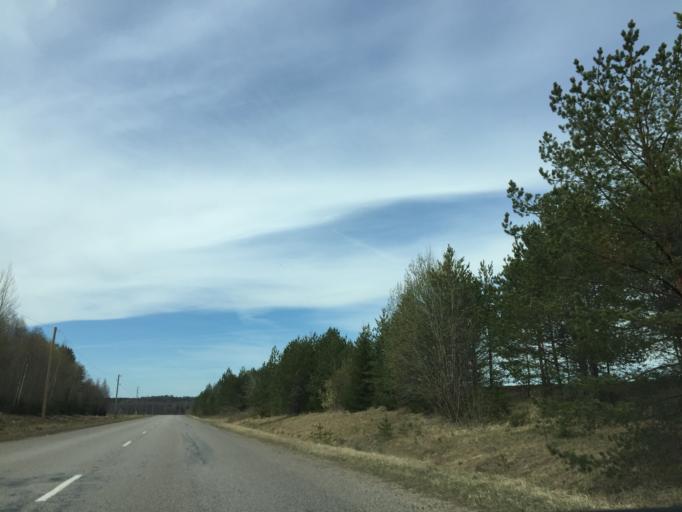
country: LV
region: Valkas Rajons
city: Valka
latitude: 57.7893
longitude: 25.8920
